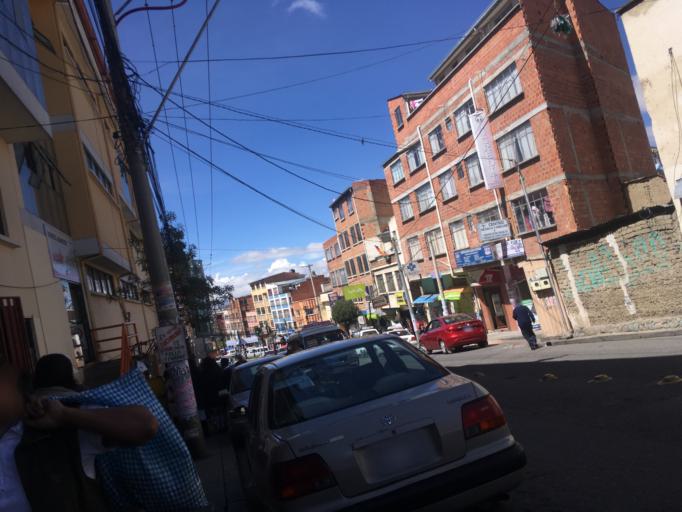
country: BO
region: La Paz
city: La Paz
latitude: -16.4950
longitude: -68.1169
